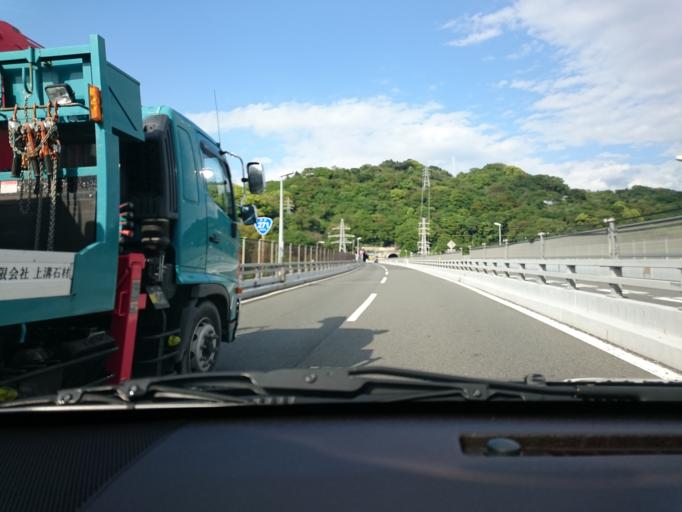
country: JP
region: Kanagawa
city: Odawara
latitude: 35.2902
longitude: 139.2004
